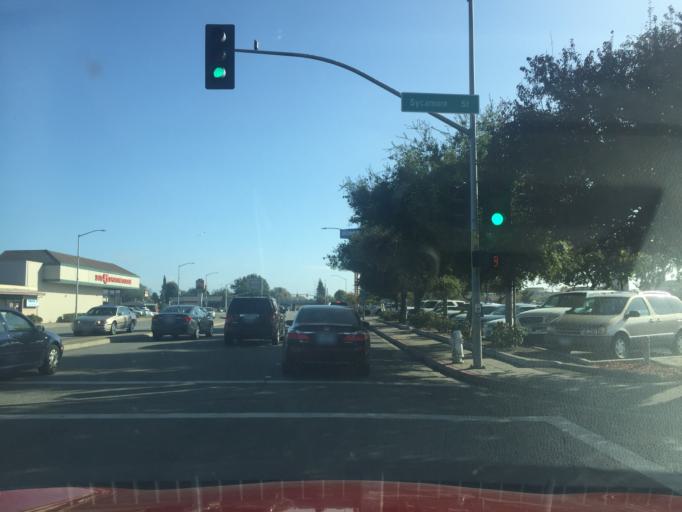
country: US
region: California
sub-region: Alameda County
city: San Lorenzo
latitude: 37.6887
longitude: -122.1302
